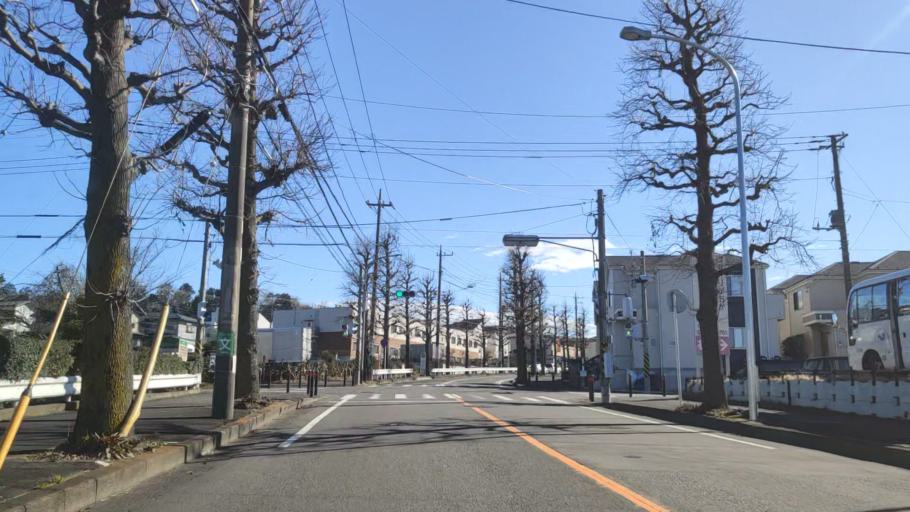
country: JP
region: Tokyo
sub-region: Machida-shi
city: Machida
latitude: 35.5192
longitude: 139.5077
